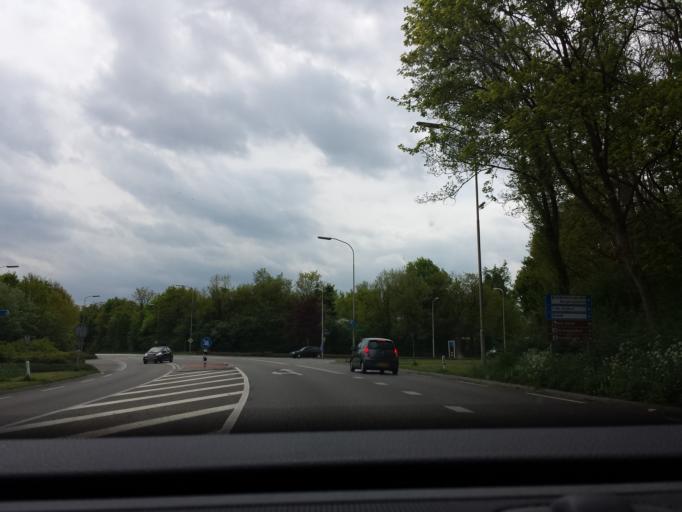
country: NL
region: Gelderland
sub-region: Gemeente Montferland
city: s-Heerenberg
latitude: 51.8843
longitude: 6.2507
